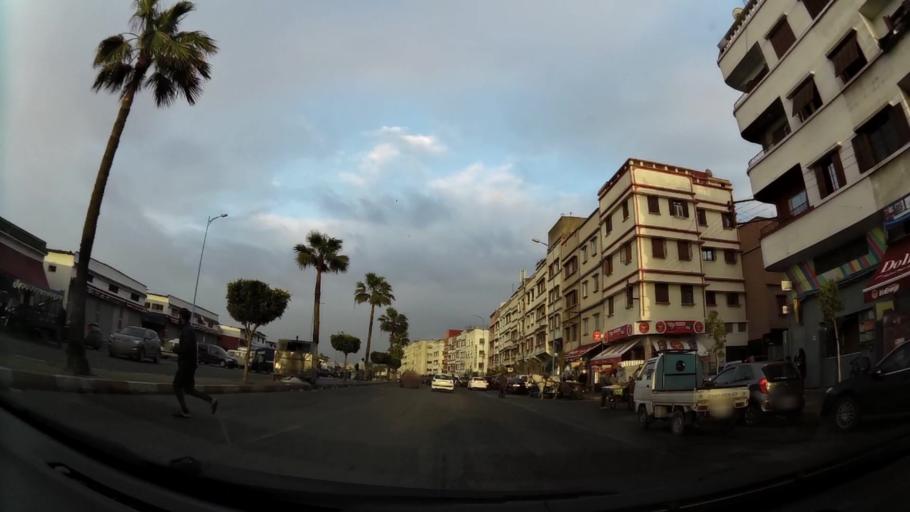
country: MA
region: Grand Casablanca
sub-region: Casablanca
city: Casablanca
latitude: 33.5618
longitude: -7.6000
